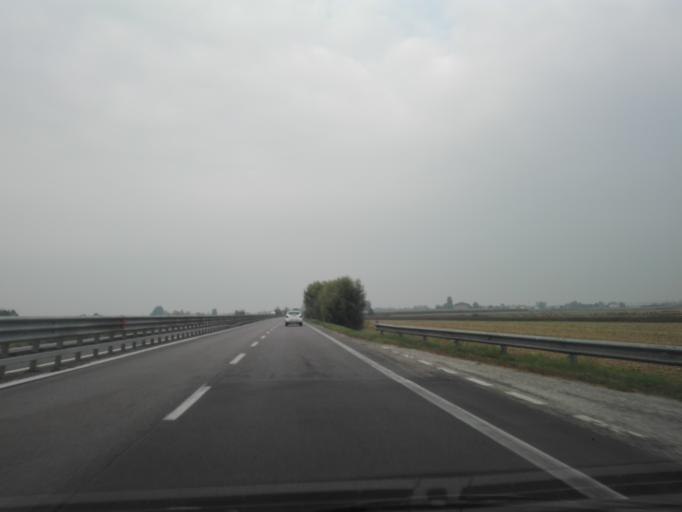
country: IT
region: Veneto
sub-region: Provincia di Verona
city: Villa Bartolomea
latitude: 45.1539
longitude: 11.3284
